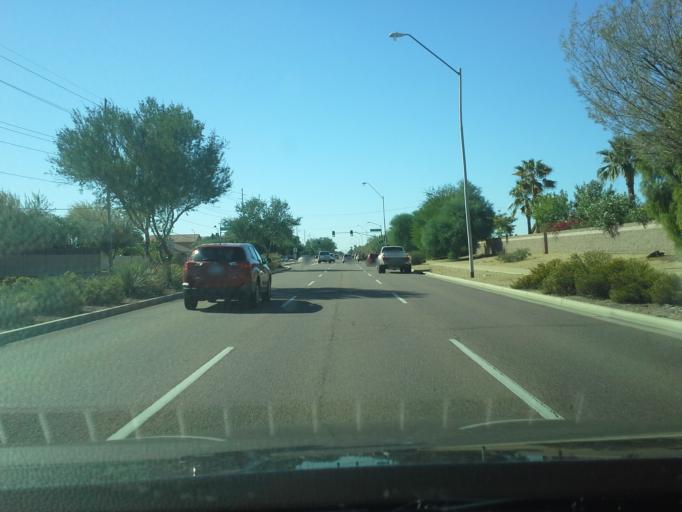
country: US
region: Arizona
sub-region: Maricopa County
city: Paradise Valley
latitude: 33.6406
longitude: -111.9671
